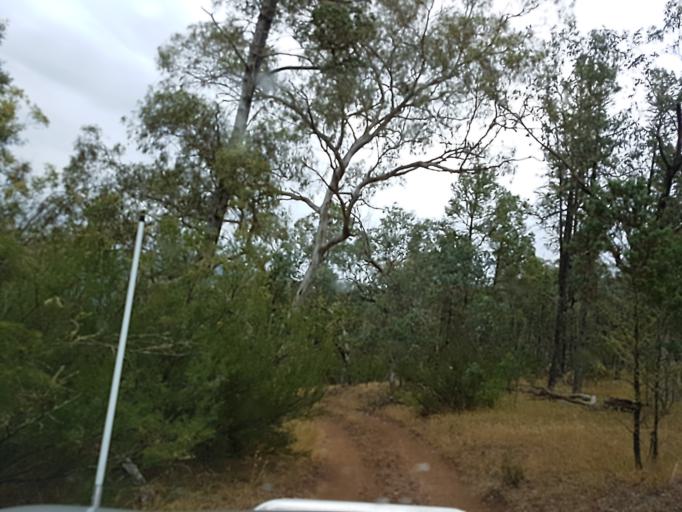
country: AU
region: New South Wales
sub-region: Snowy River
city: Jindabyne
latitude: -36.9431
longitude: 148.3953
